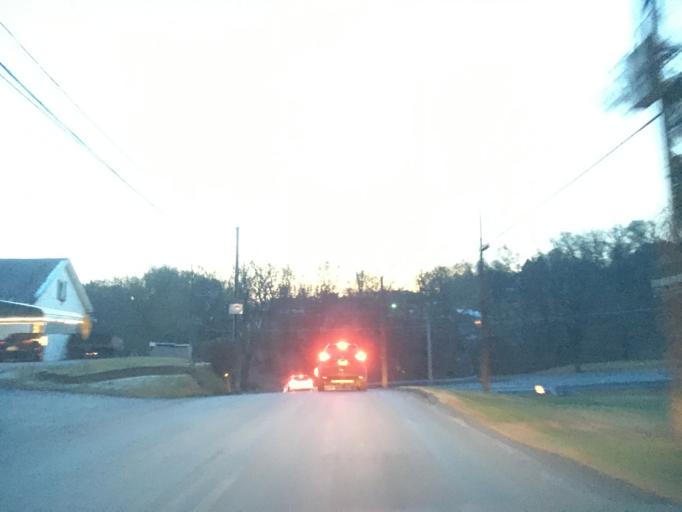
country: US
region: Pennsylvania
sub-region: Northampton County
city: Cherryville
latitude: 40.7383
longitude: -75.5443
